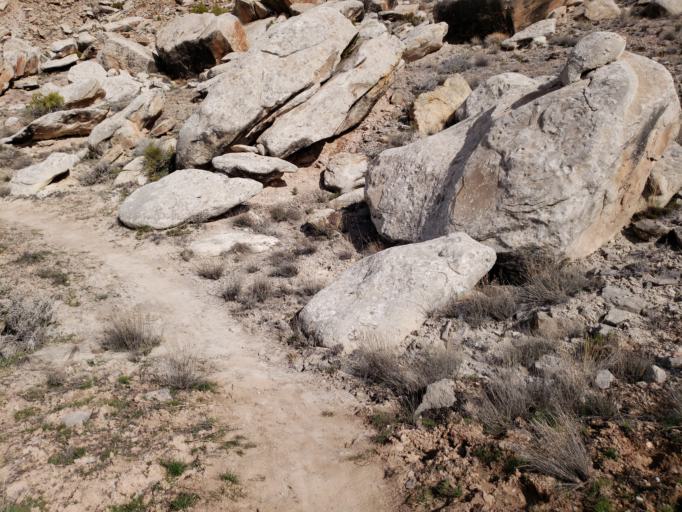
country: US
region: Colorado
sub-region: Mesa County
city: Loma
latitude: 39.1931
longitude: -108.8813
